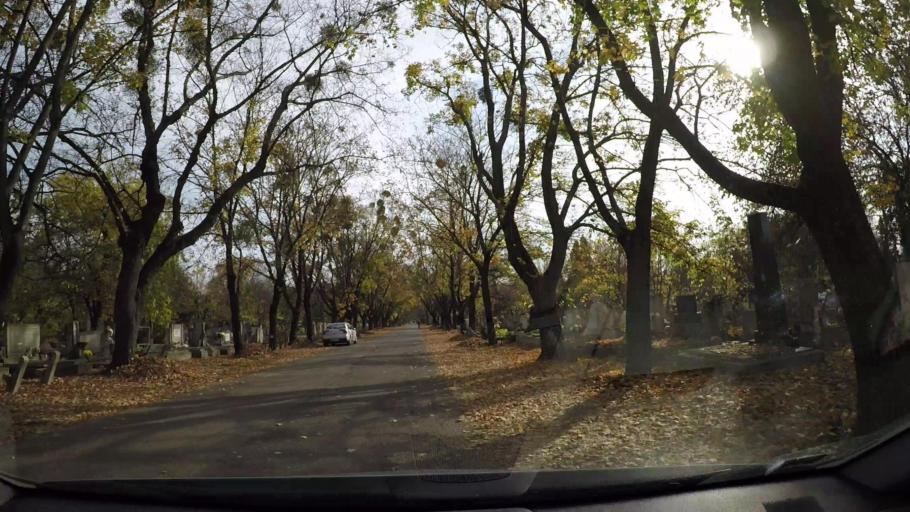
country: HU
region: Budapest
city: Budapest X. keruelet
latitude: 47.4714
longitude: 19.1853
